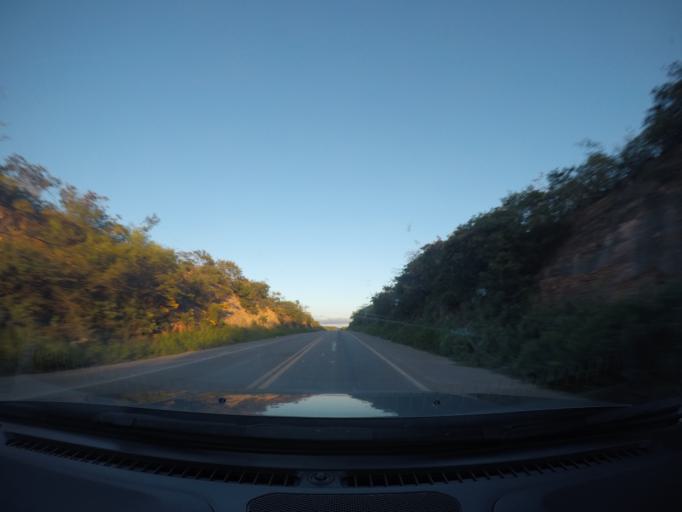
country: BR
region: Bahia
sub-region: Seabra
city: Seabra
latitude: -12.3916
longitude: -41.9113
